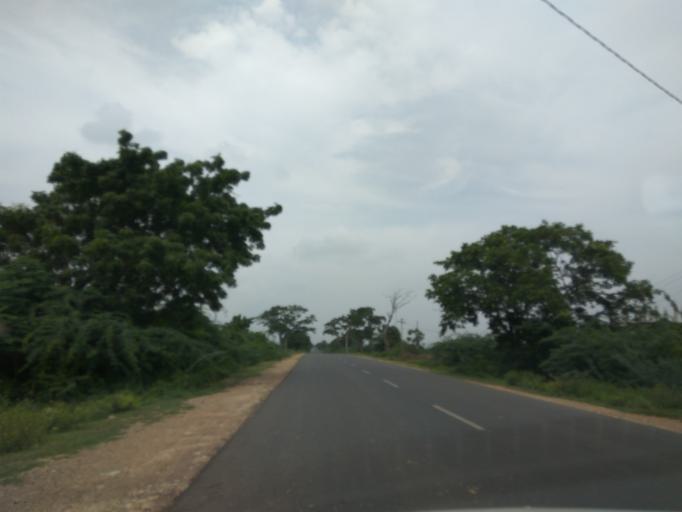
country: IN
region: Andhra Pradesh
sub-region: Prakasam
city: Cumbum
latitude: 15.5044
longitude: 79.0860
